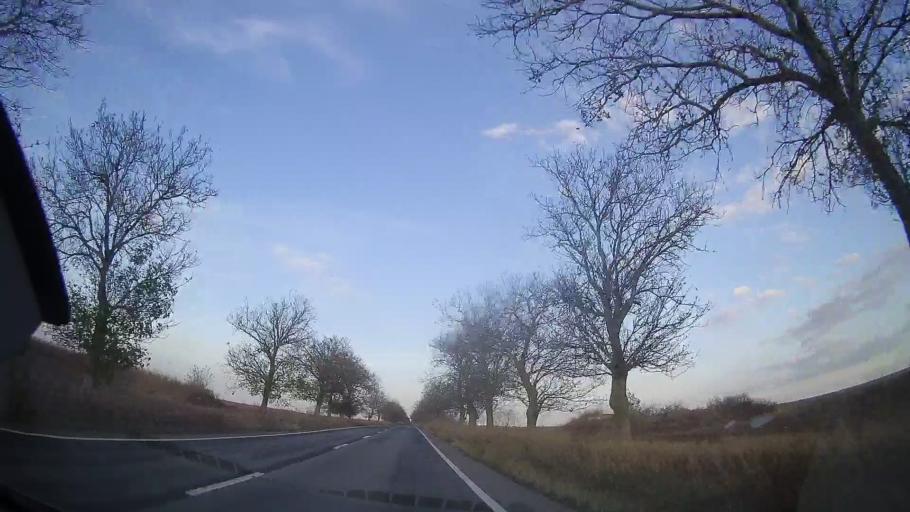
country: RO
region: Constanta
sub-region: Comuna Chirnogeni
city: Chirnogeni
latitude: 43.8621
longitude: 28.2603
